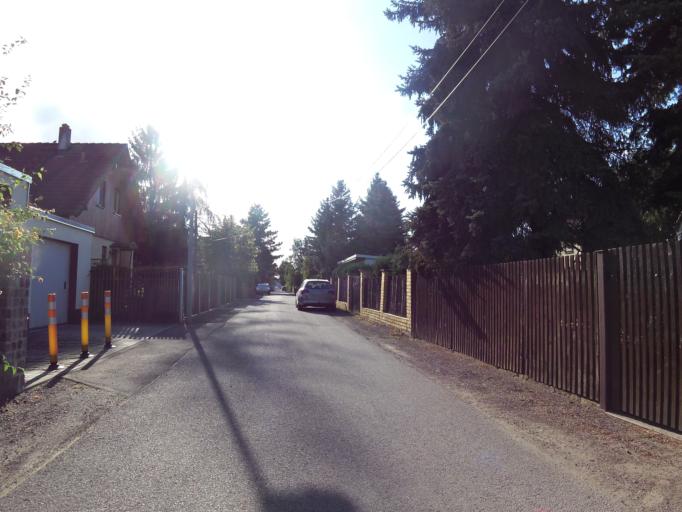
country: DE
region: Saxony
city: Markranstadt
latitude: 51.3475
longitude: 12.2739
